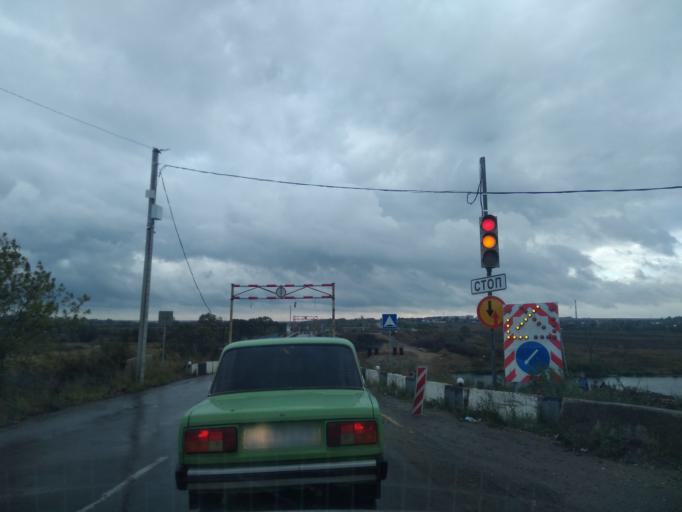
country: RU
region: Tula
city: Yefremov
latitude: 53.1303
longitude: 38.1194
